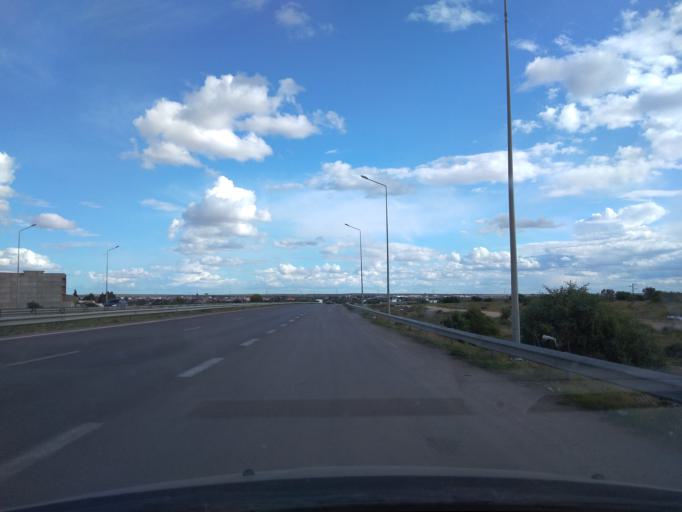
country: TN
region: Susah
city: Masakin
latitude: 35.7103
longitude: 10.5596
